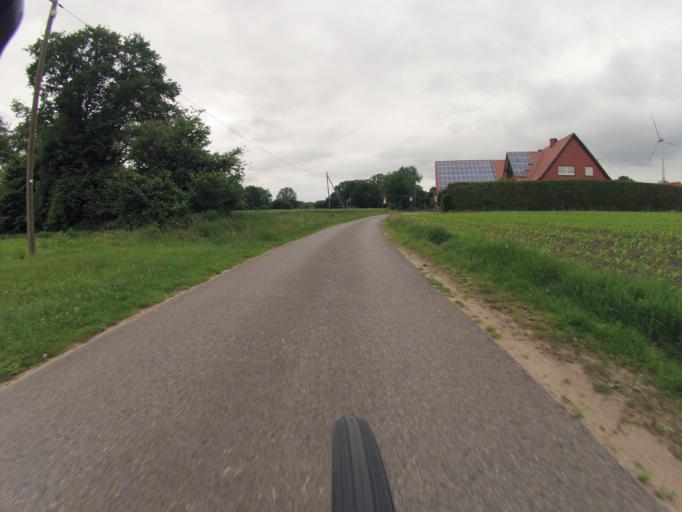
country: DE
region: North Rhine-Westphalia
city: Emsdetten
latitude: 52.2117
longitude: 7.5588
